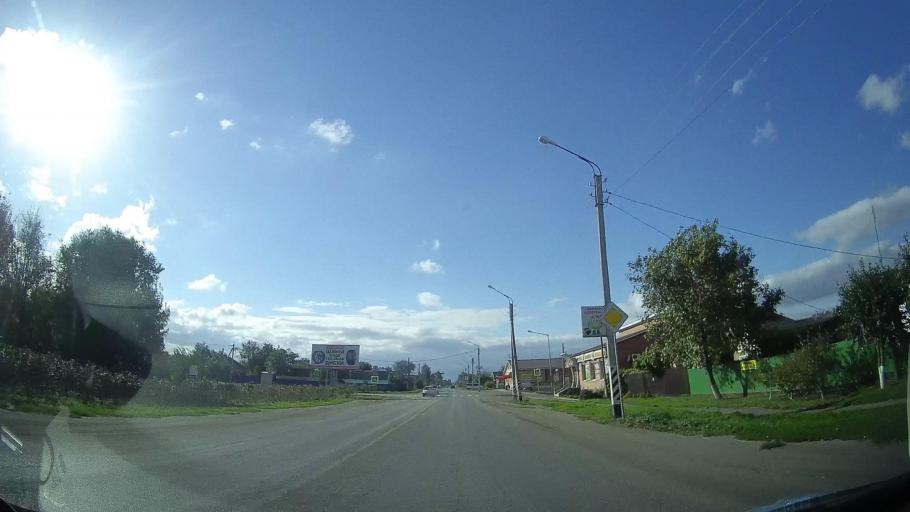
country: RU
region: Rostov
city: Tselina
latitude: 46.5300
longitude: 41.0319
